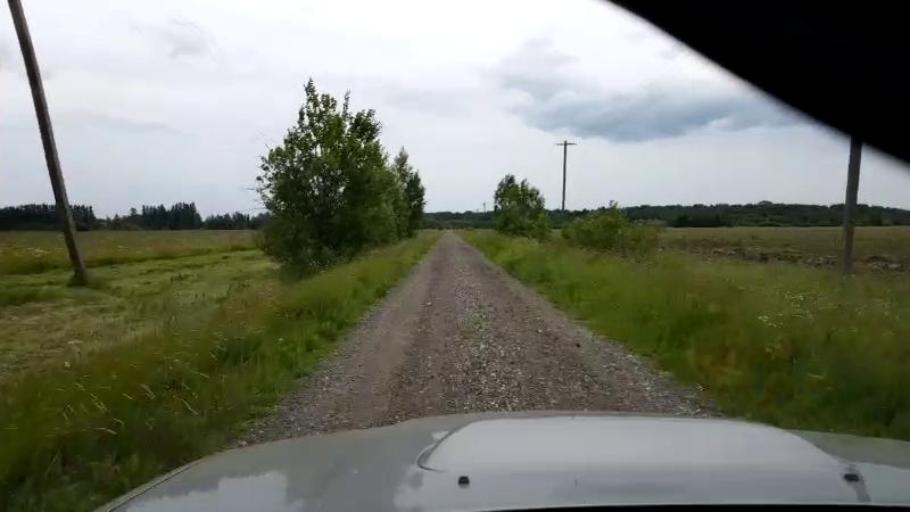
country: EE
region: Paernumaa
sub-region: Halinga vald
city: Parnu-Jaagupi
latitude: 58.5303
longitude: 24.6122
